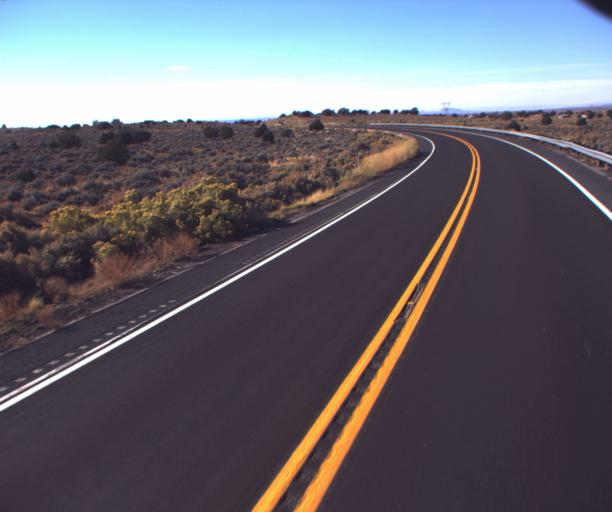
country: US
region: Arizona
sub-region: Coconino County
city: Kaibito
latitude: 36.6130
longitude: -110.9242
